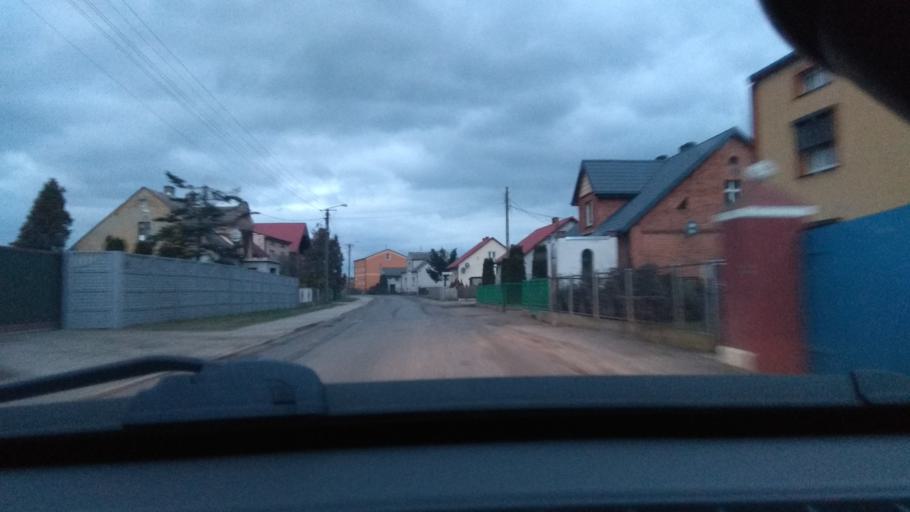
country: PL
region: Lodz Voivodeship
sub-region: Powiat wieruszowski
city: Wieruszow
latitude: 51.3044
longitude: 18.0811
